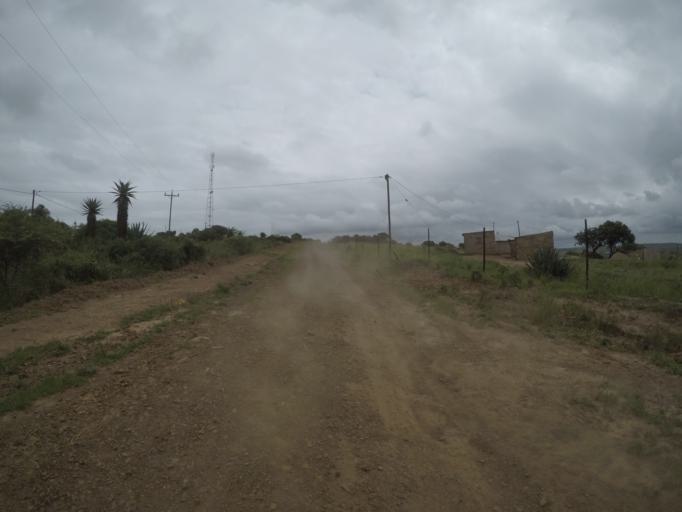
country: ZA
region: KwaZulu-Natal
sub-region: uThungulu District Municipality
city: Empangeni
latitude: -28.6034
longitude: 31.8369
